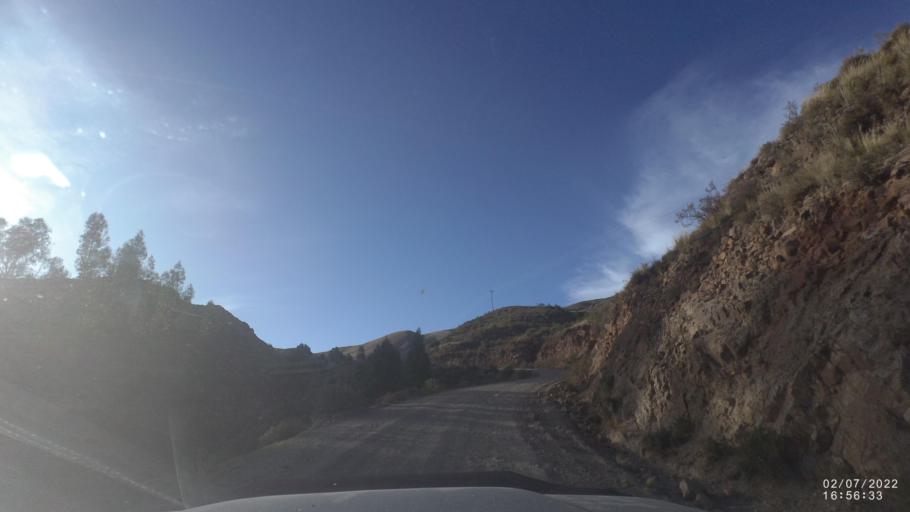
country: BO
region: Cochabamba
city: Irpa Irpa
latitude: -17.9551
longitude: -66.5439
